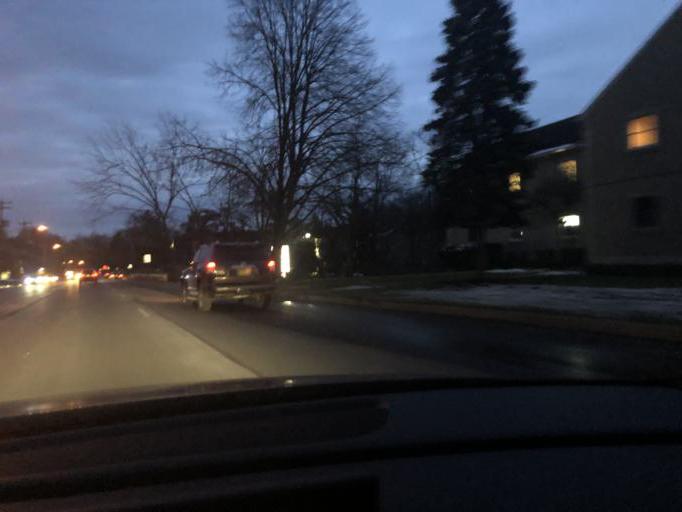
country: US
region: New Jersey
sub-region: Morris County
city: Florham Park
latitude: 40.7866
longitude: -74.3867
